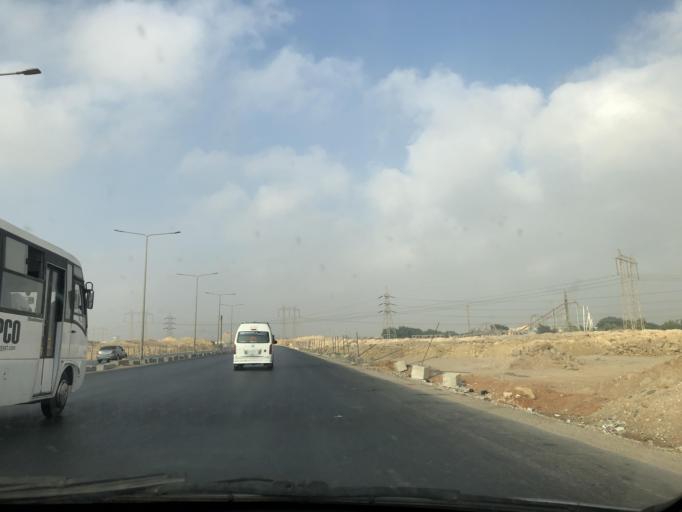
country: EG
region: Al Jizah
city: Al Jizah
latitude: 29.9670
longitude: 31.0672
